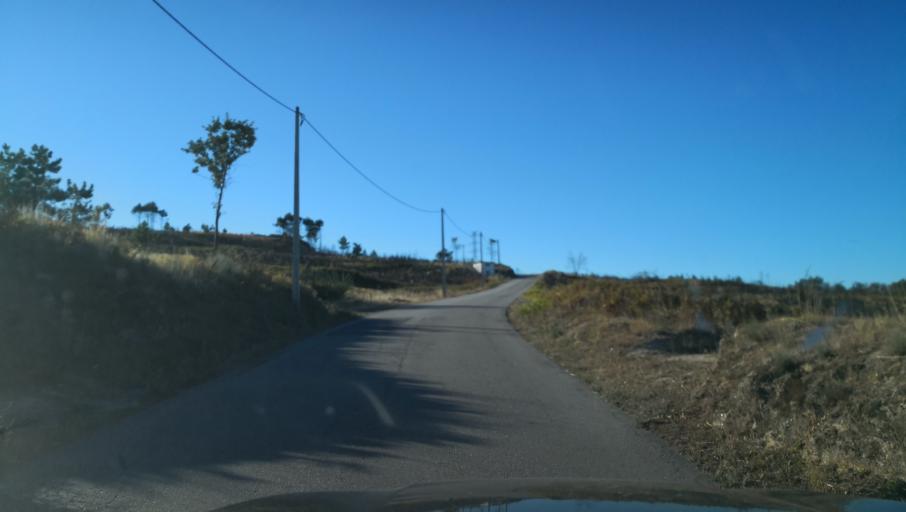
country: PT
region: Vila Real
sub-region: Sabrosa
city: Sabrosa
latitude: 41.3260
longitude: -7.6132
